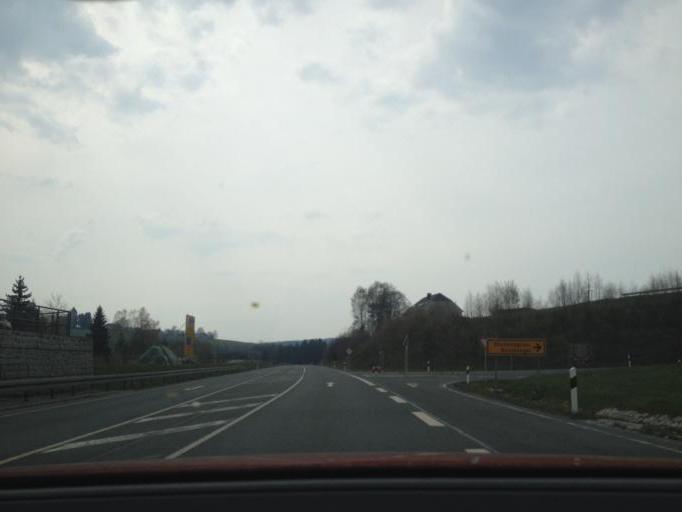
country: DE
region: Bavaria
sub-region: Upper Franconia
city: Bischofsgrun
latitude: 50.0568
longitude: 11.8047
